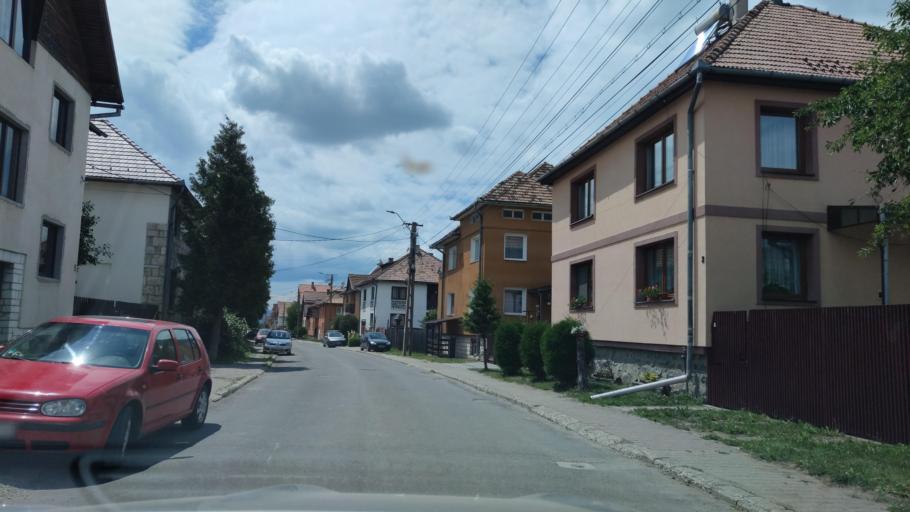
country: RO
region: Harghita
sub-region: Municipiul Gheorgheni
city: Gheorgheni
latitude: 46.7165
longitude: 25.5959
